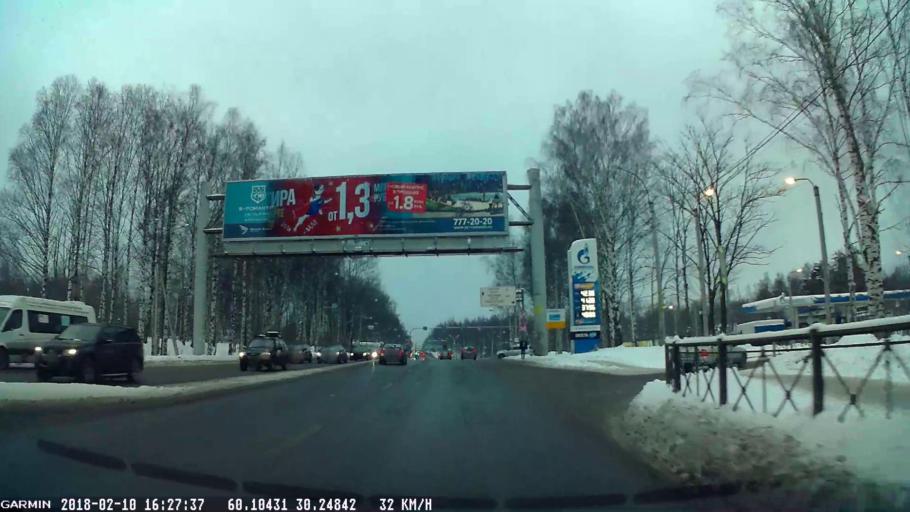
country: RU
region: St.-Petersburg
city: Pargolovo
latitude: 60.1045
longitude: 30.2483
